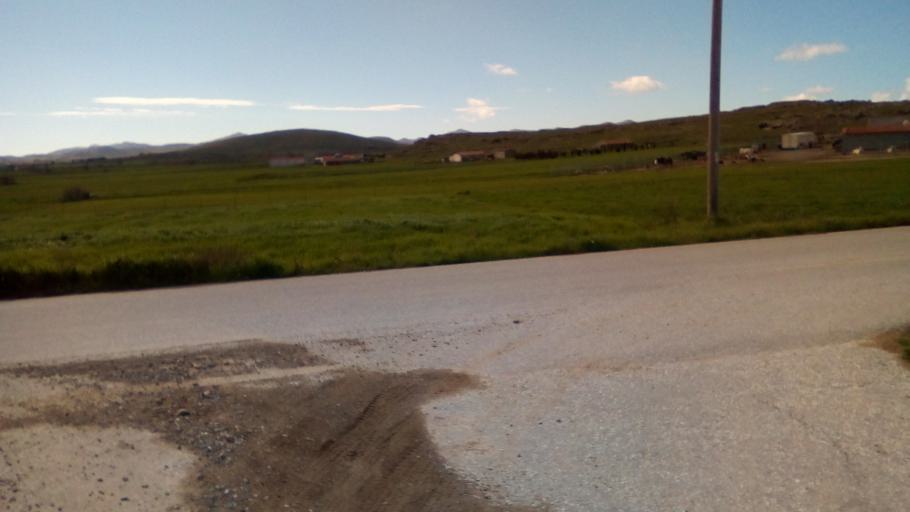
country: GR
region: North Aegean
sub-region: Nomos Lesvou
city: Myrina
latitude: 39.9284
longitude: 25.2327
